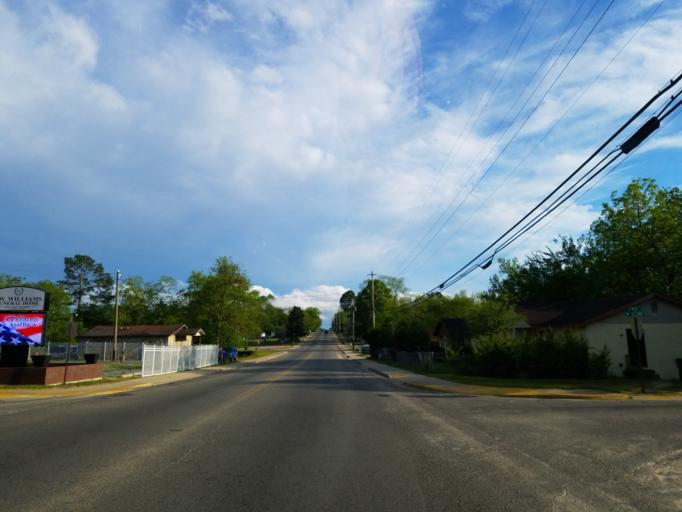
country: US
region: Georgia
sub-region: Crisp County
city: Cordele
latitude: 31.9626
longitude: -83.7879
